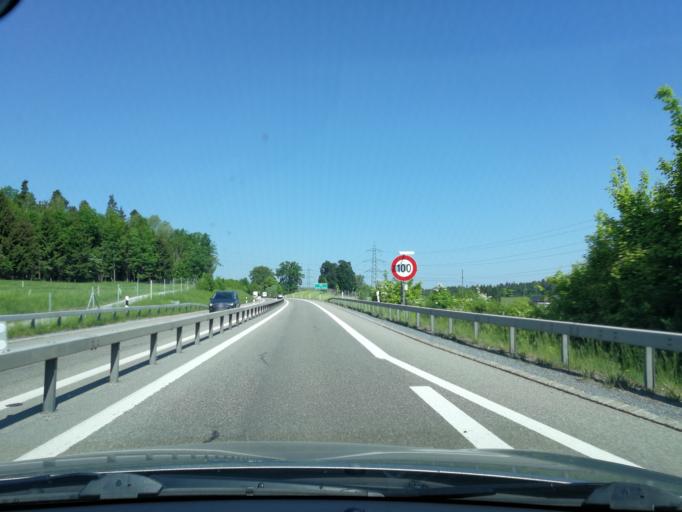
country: CH
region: Zurich
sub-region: Bezirk Uster
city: Esslingen
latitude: 47.2941
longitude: 8.7137
